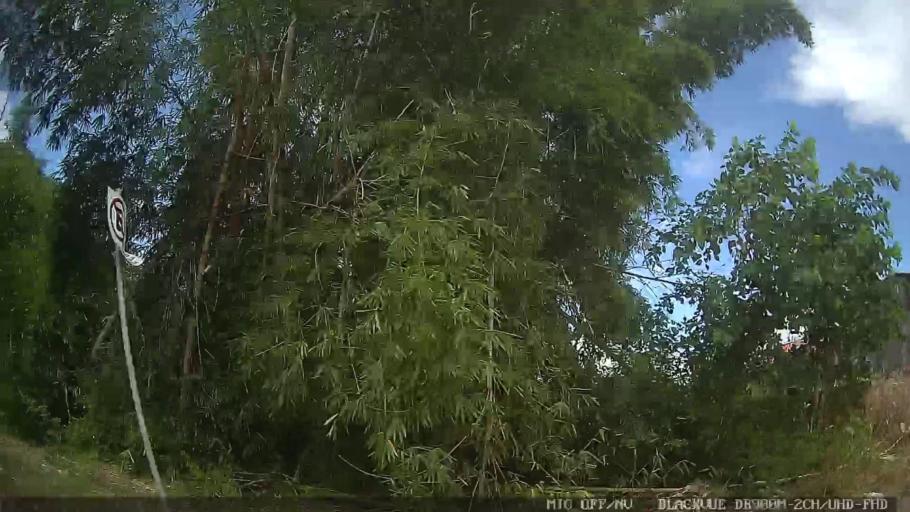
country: BR
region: Sao Paulo
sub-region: Conchas
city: Conchas
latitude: -23.0116
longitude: -48.0037
